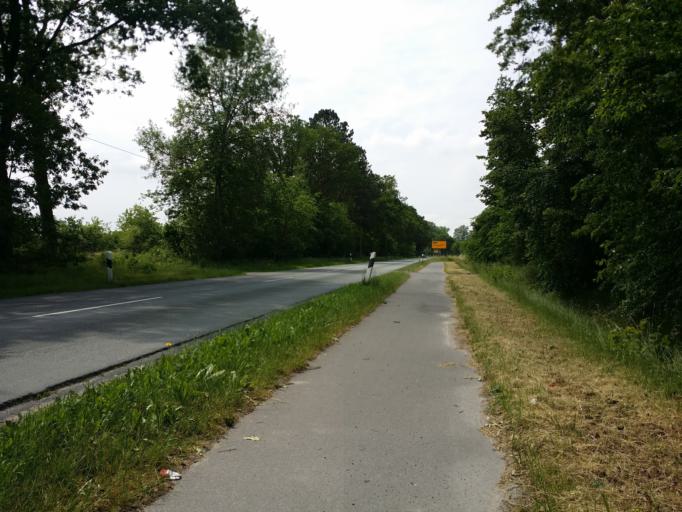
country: DE
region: Lower Saxony
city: Friedeburg
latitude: 53.4151
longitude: 7.8956
